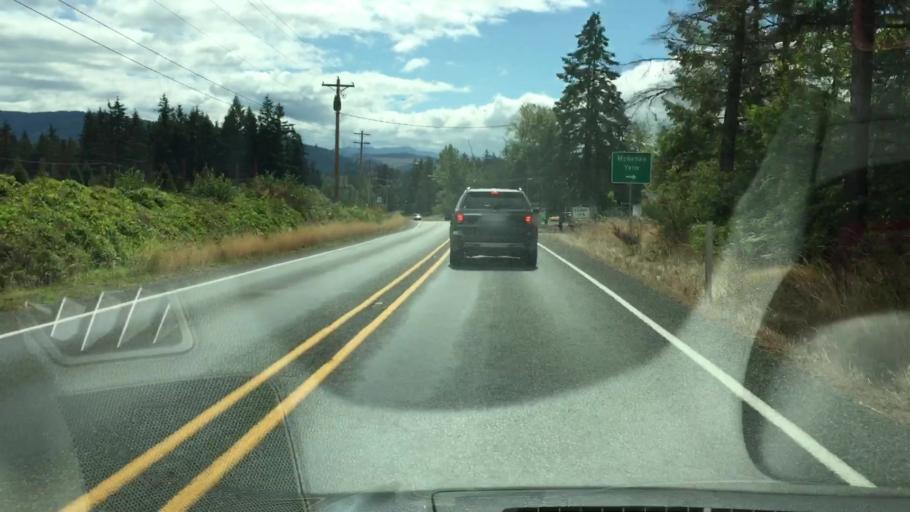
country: US
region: Washington
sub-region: Pierce County
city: Eatonville
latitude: 46.8892
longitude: -122.3000
